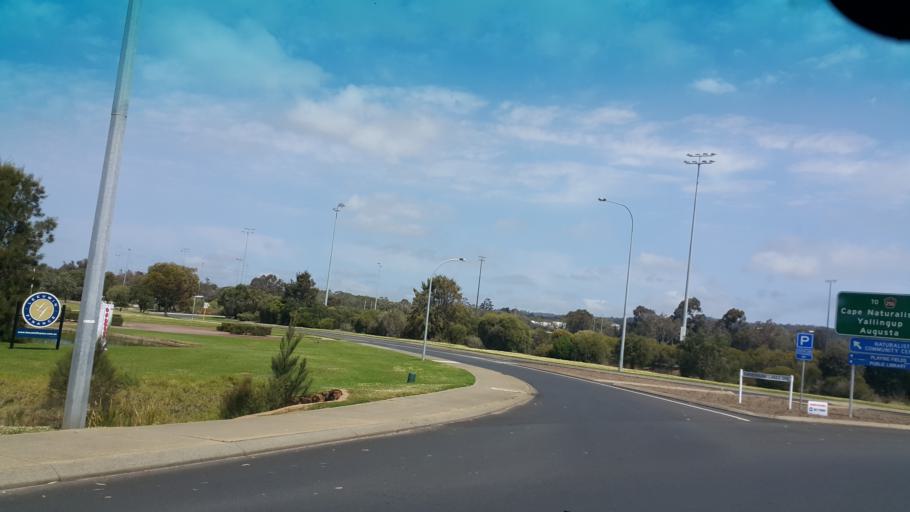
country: AU
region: Western Australia
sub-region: Busselton
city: Dunsborough
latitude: -33.6181
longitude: 115.1076
